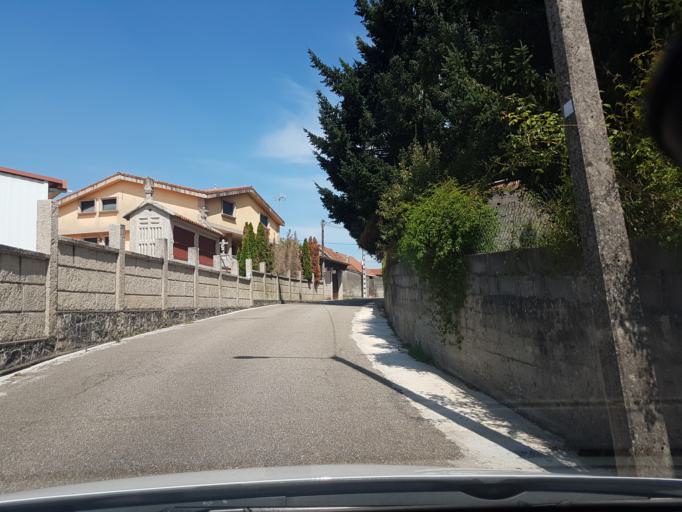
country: ES
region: Galicia
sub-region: Provincia de Pontevedra
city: Porrino
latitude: 42.2009
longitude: -8.6206
